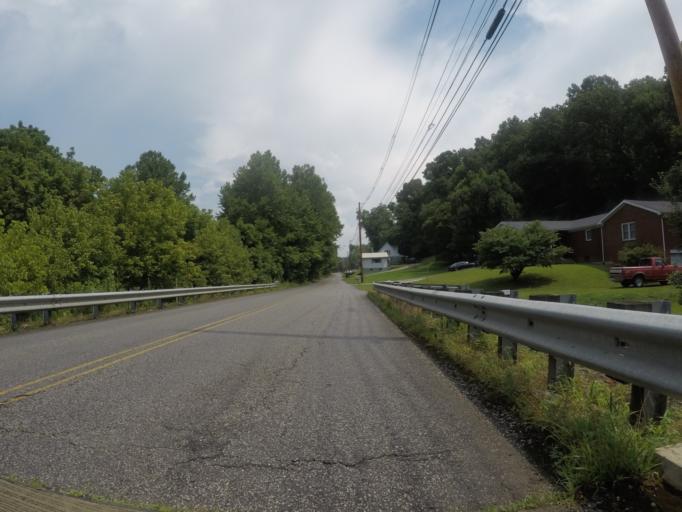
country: US
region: Kentucky
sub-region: Boyd County
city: Westwood
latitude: 38.4706
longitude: -82.6710
